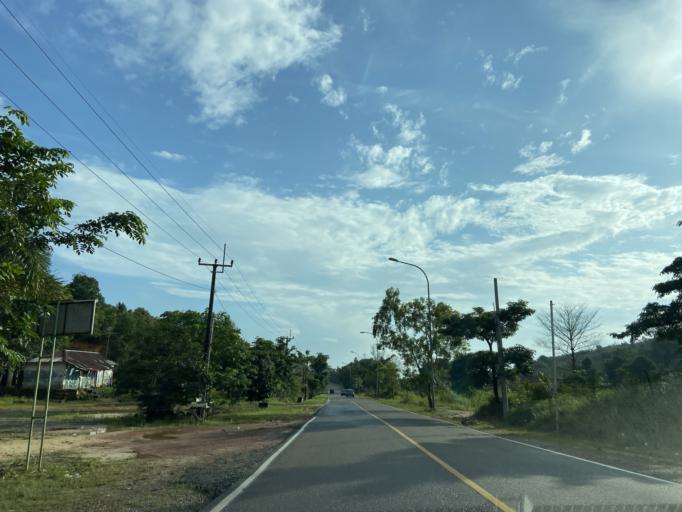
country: SG
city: Singapore
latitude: 0.9610
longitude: 104.0550
